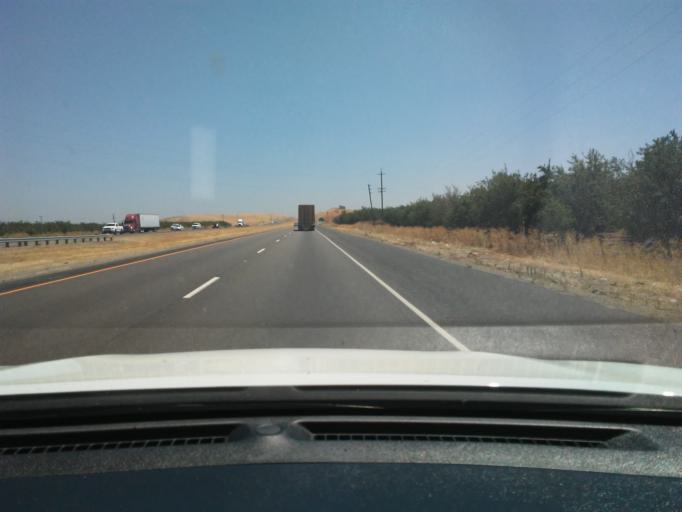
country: US
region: California
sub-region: Stanislaus County
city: Patterson
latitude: 37.4035
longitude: -121.1427
